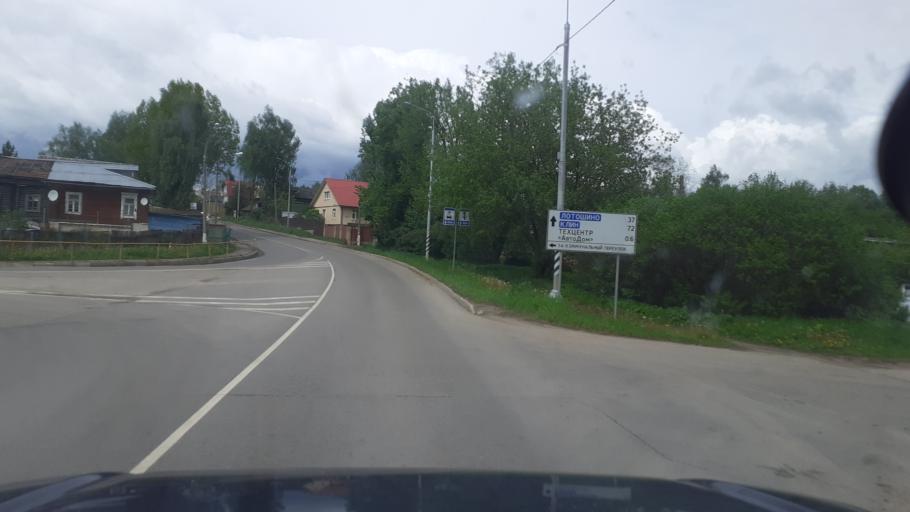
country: RU
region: Moskovskaya
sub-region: Volokolamskiy Rayon
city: Volokolamsk
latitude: 56.0411
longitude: 35.9553
